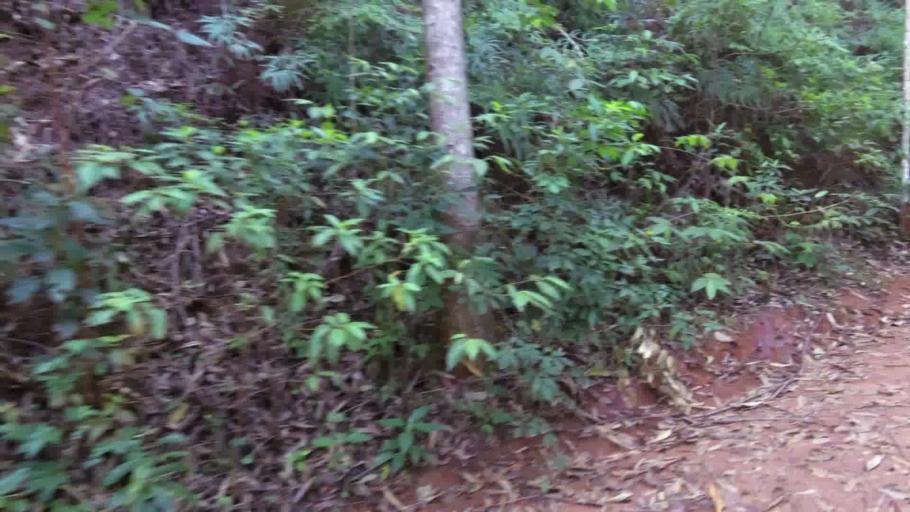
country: BR
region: Espirito Santo
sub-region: Alfredo Chaves
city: Alfredo Chaves
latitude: -20.6066
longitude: -40.7499
